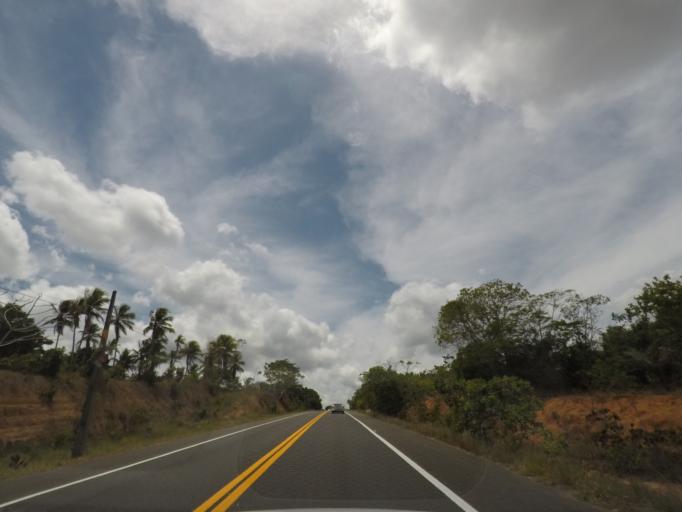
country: BR
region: Sergipe
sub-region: Indiaroba
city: Indiaroba
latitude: -11.5506
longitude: -37.5705
